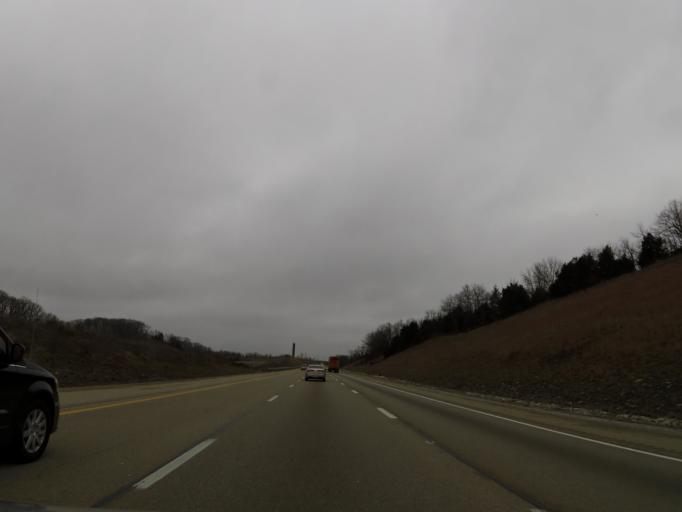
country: US
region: Kentucky
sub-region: Grant County
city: Williamstown
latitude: 38.5341
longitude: -84.5906
